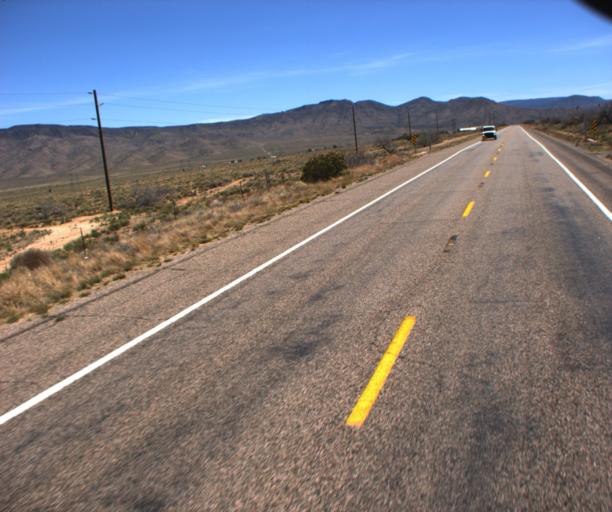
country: US
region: Arizona
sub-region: Mohave County
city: New Kingman-Butler
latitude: 35.4151
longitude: -113.7899
